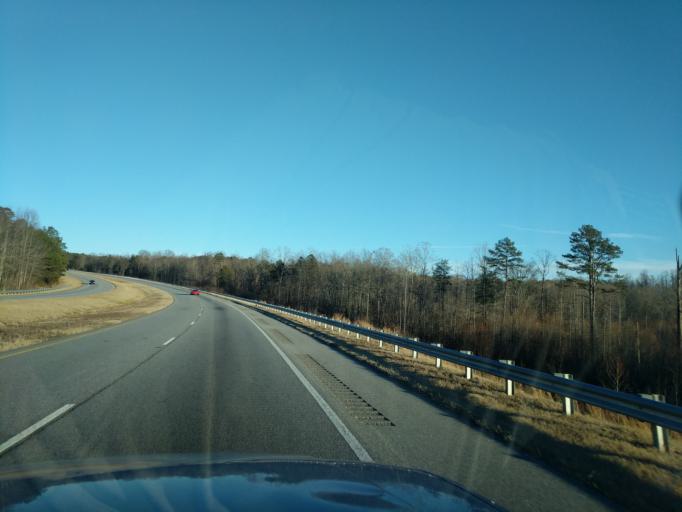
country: US
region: Georgia
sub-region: Stephens County
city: Toccoa
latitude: 34.5319
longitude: -83.3082
